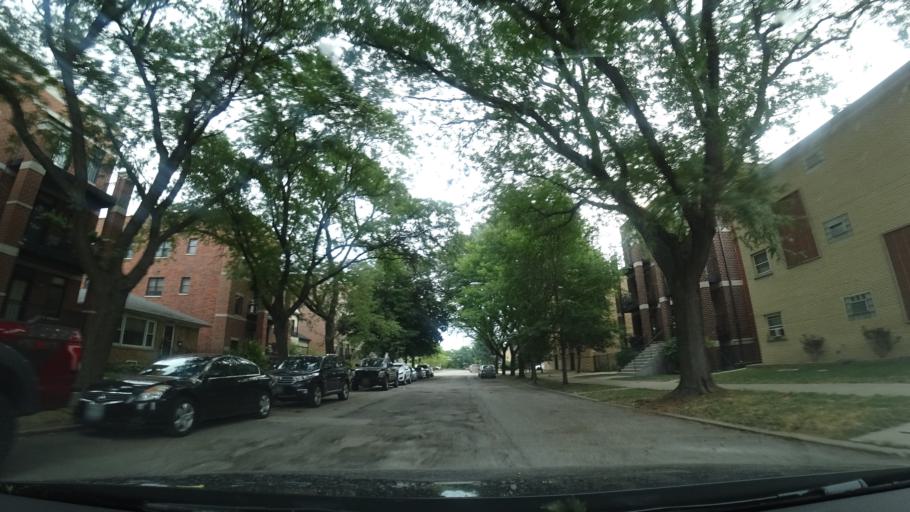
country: US
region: Illinois
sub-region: Cook County
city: Harwood Heights
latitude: 41.9709
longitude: -87.7664
